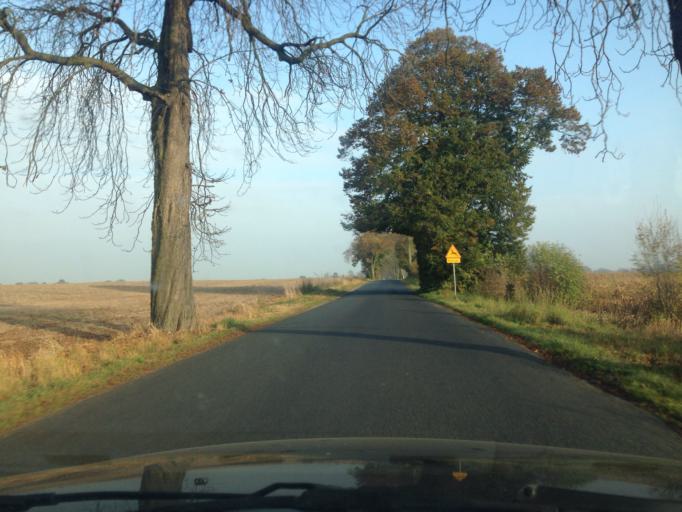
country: PL
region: Kujawsko-Pomorskie
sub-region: Powiat wabrzeski
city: Debowa Laka
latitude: 53.2589
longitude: 19.0696
